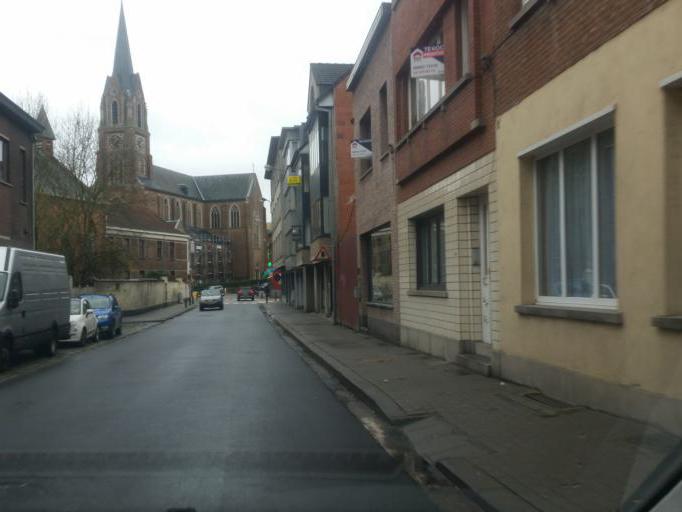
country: BE
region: Flanders
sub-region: Provincie Vlaams-Brabant
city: Grimbergen
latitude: 50.9113
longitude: 4.3559
